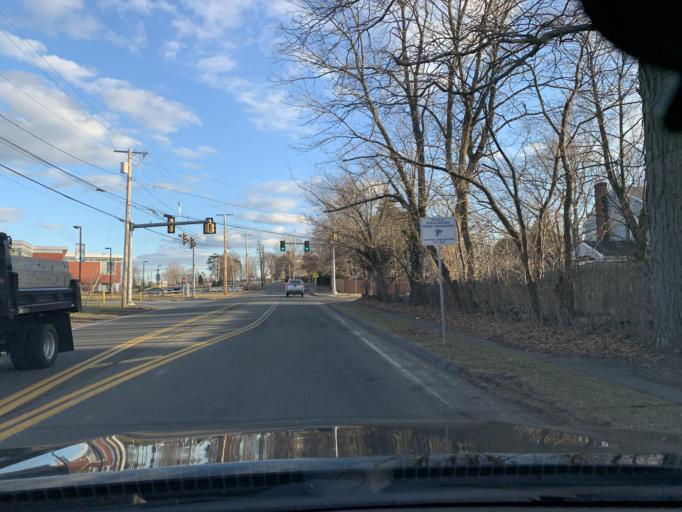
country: US
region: Massachusetts
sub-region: Essex County
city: Middleton
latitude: 42.5923
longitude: -70.9807
